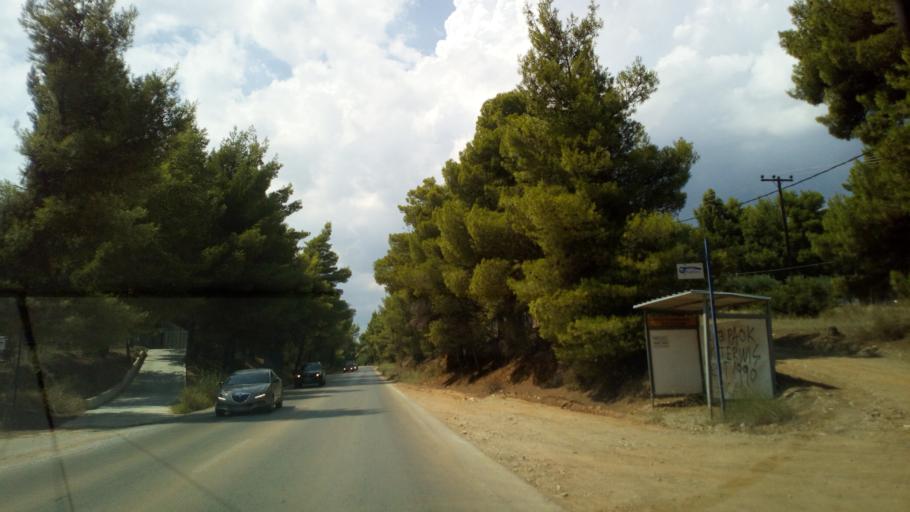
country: GR
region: Central Macedonia
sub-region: Nomos Chalkidikis
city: Nikiti
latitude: 40.2289
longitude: 23.6328
